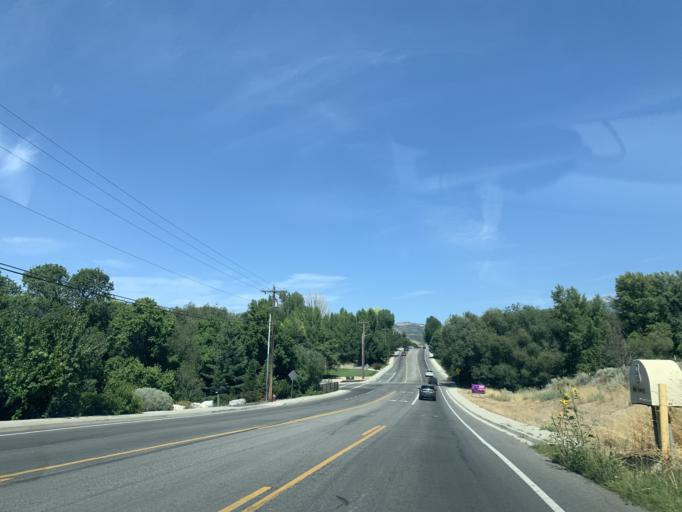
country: US
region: Utah
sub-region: Utah County
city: Lehi
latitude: 40.4064
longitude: -111.8303
